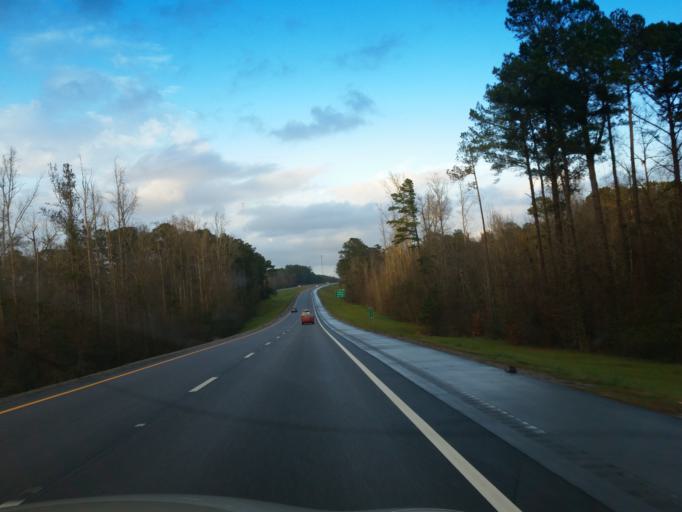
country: US
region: Mississippi
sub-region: Jones County
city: Sharon
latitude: 31.9549
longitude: -88.9768
